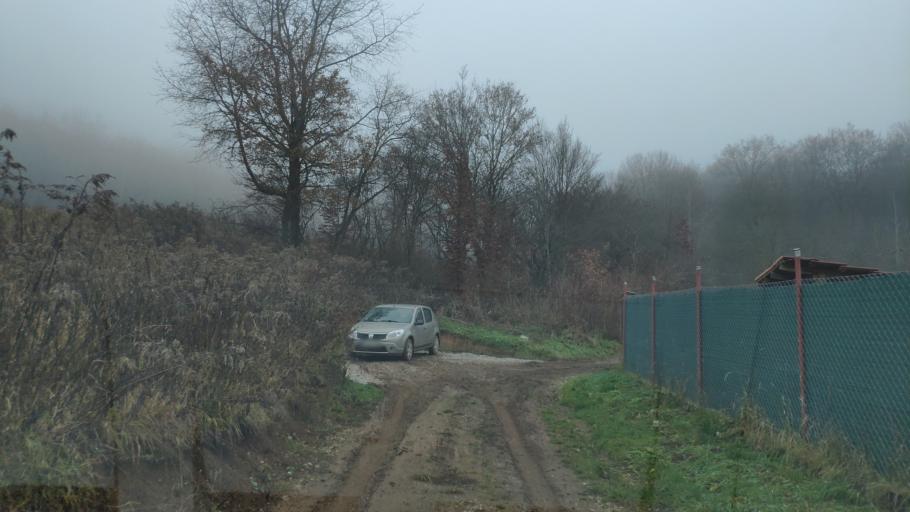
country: SK
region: Banskobystricky
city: Revuca
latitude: 48.6523
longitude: 20.2572
